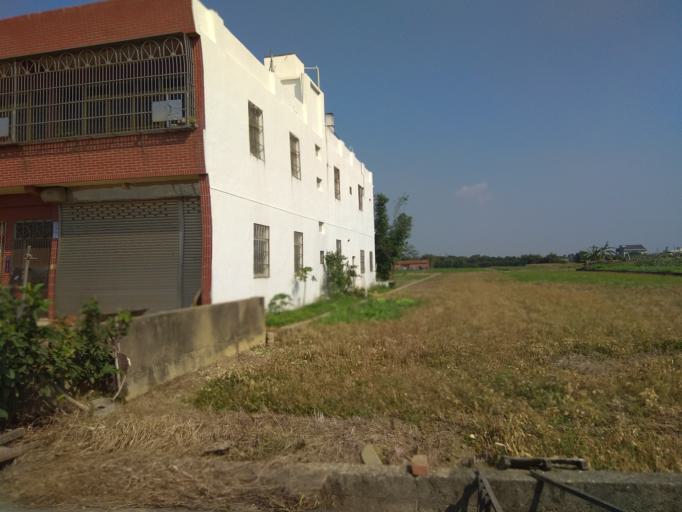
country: TW
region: Taiwan
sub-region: Hsinchu
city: Zhubei
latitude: 24.9940
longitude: 121.0669
